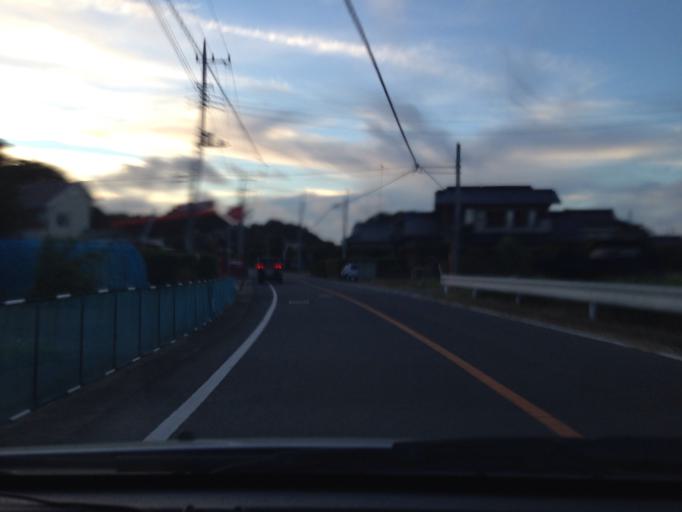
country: JP
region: Ibaraki
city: Inashiki
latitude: 36.0087
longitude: 140.3650
